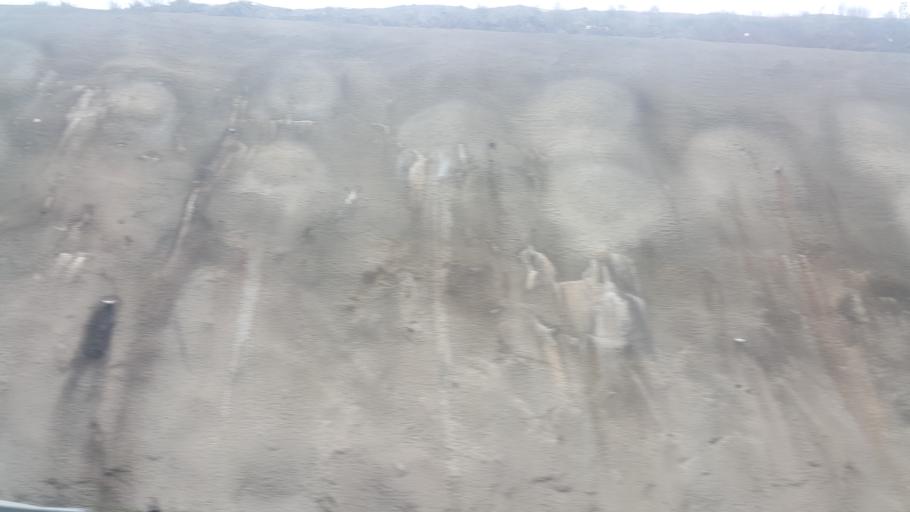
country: TR
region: Nigde
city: Ciftehan
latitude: 37.5566
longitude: 34.7673
